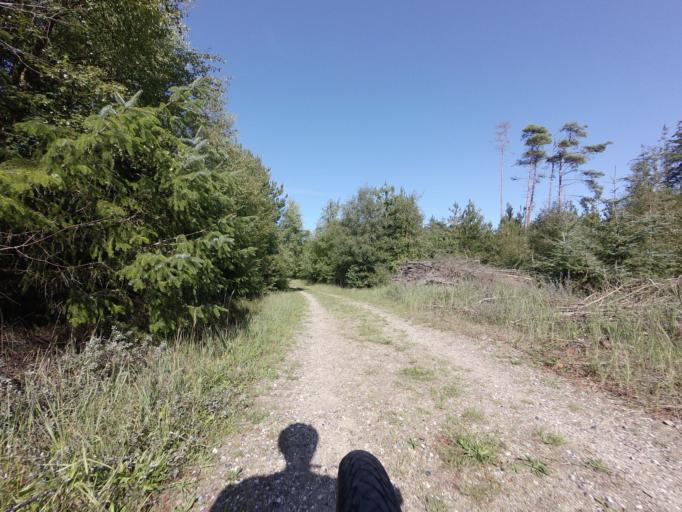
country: DK
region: North Denmark
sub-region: Hjorring Kommune
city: Hirtshals
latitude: 57.5806
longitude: 10.0029
